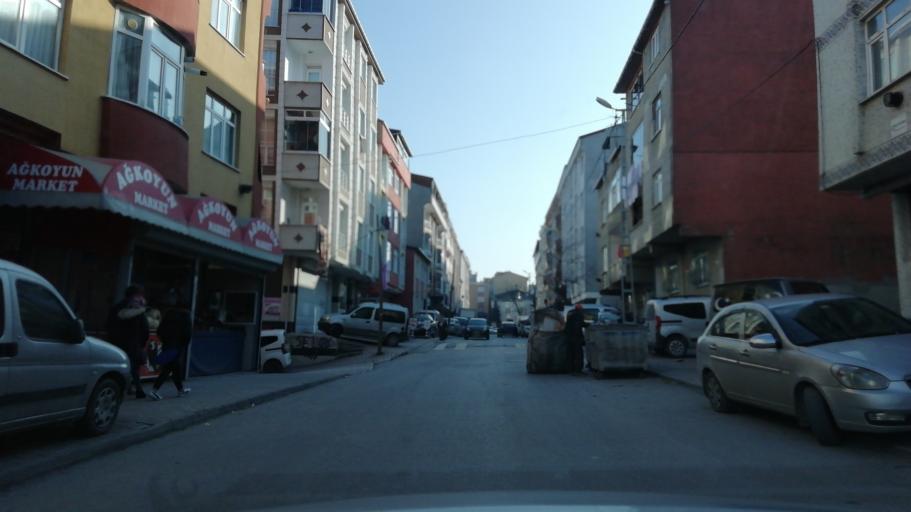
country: TR
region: Istanbul
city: Esenyurt
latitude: 41.0339
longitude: 28.6892
